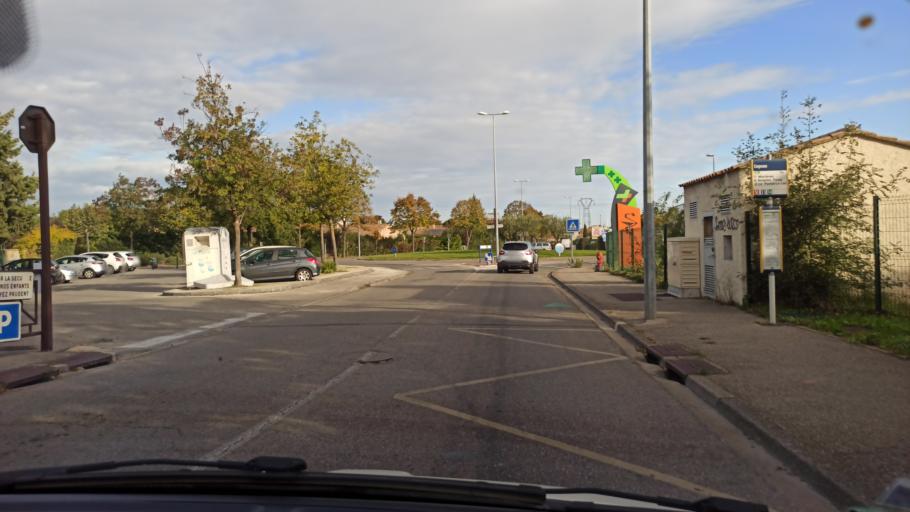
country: FR
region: Provence-Alpes-Cote d'Azur
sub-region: Departement du Vaucluse
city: Le Pontet
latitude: 43.9490
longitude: 4.8517
